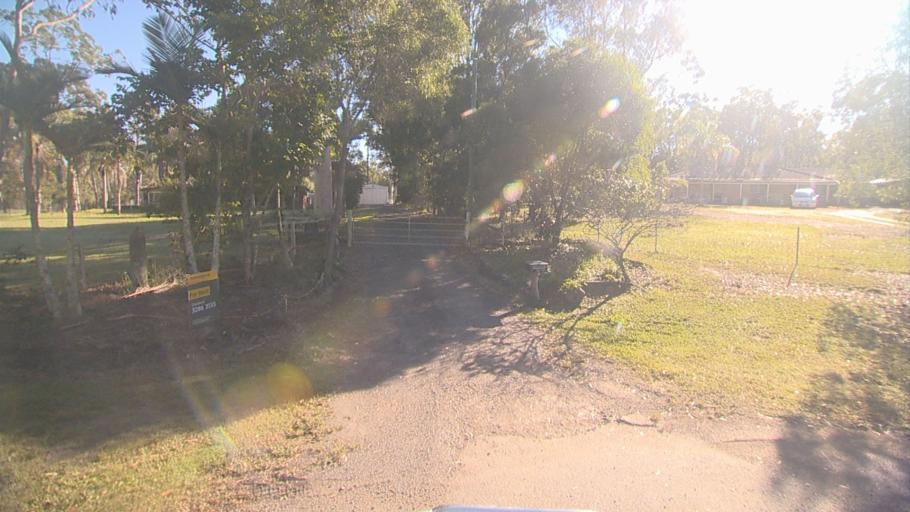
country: AU
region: Queensland
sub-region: Redland
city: Redland Bay
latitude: -27.6669
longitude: 153.2682
